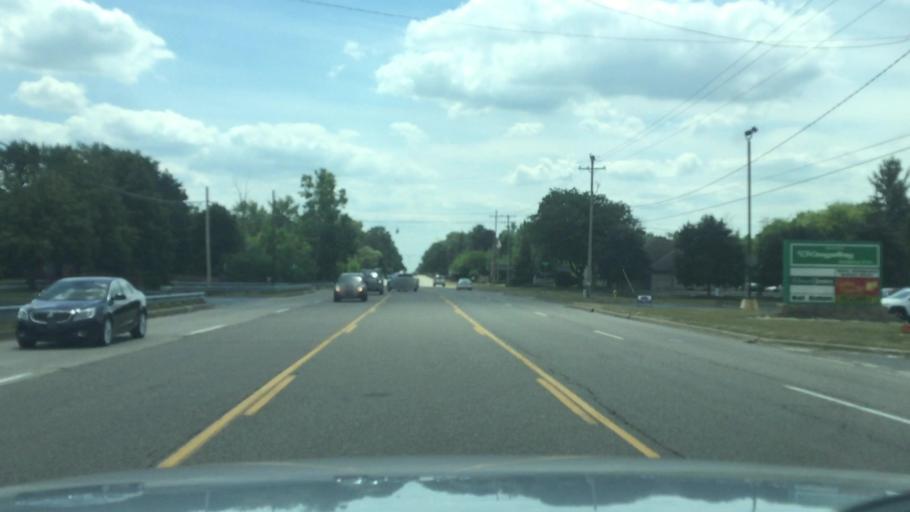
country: US
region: Michigan
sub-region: Genesee County
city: Grand Blanc
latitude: 42.9430
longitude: -83.6920
